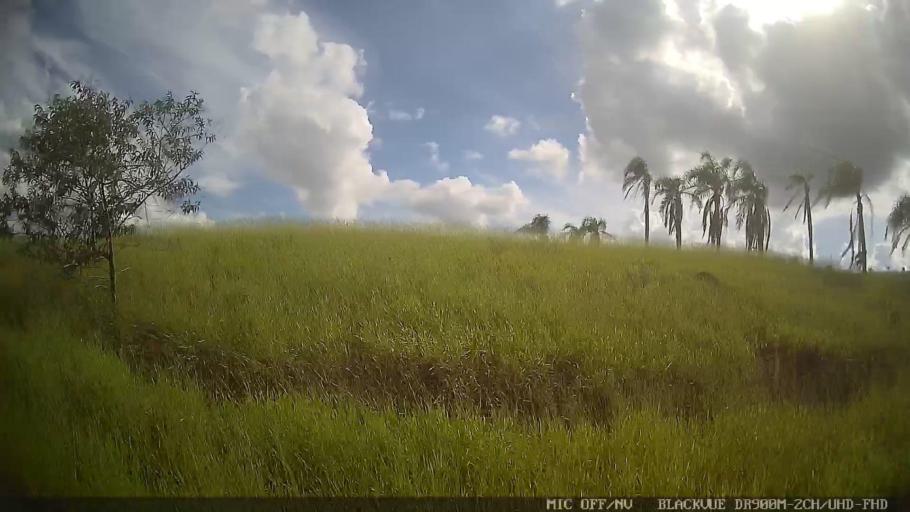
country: BR
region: Sao Paulo
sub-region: Atibaia
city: Atibaia
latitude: -23.0739
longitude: -46.5683
